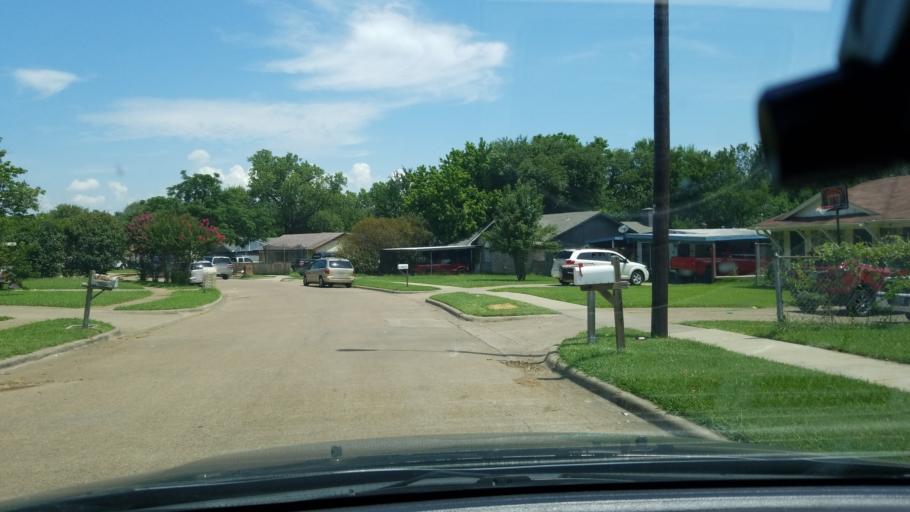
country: US
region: Texas
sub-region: Dallas County
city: Balch Springs
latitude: 32.7512
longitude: -96.6361
